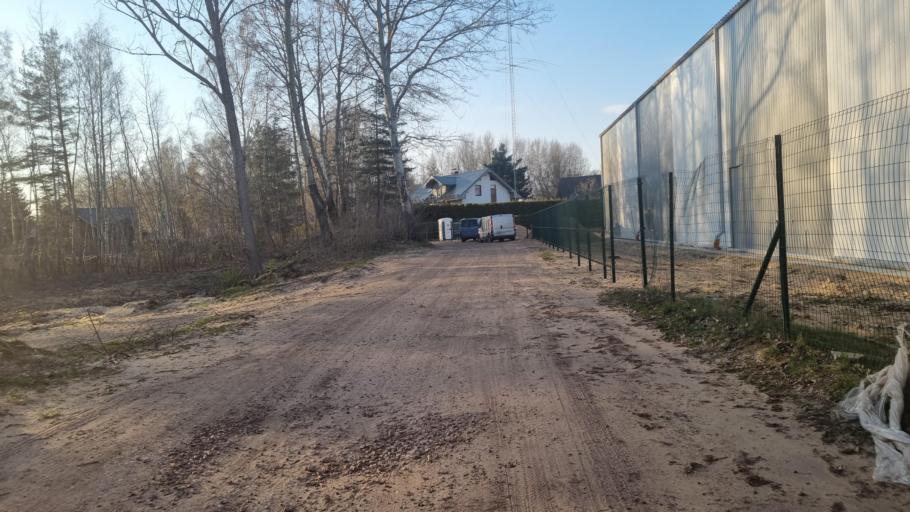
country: LV
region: Kekava
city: Balozi
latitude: 56.9105
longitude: 24.1231
